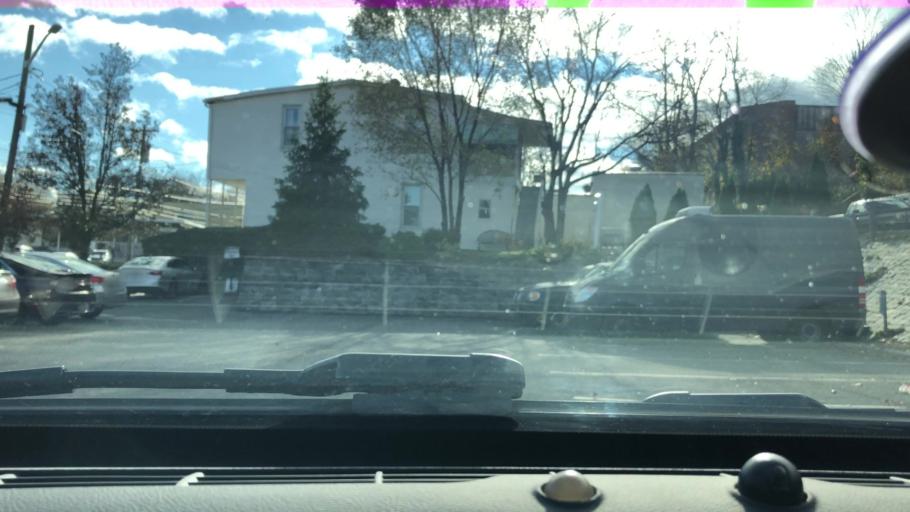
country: US
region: New York
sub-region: Westchester County
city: Greenville
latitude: 40.9755
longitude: -73.8032
